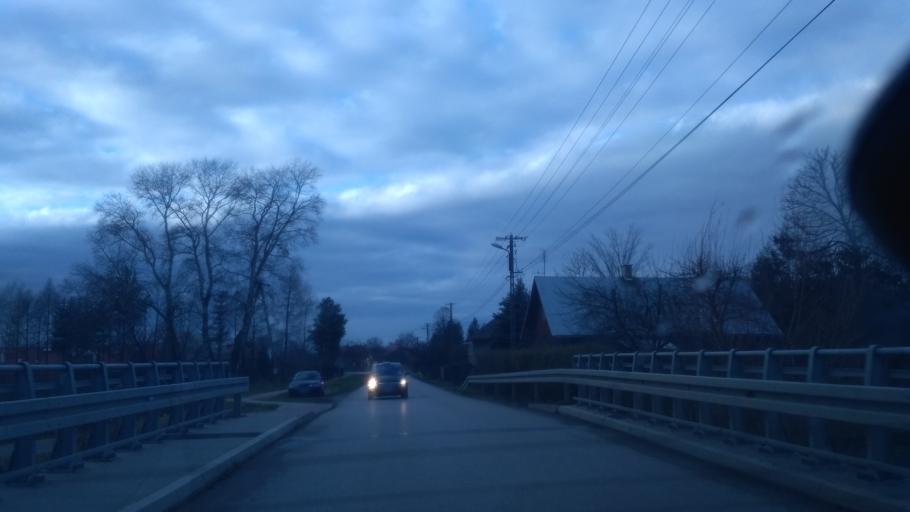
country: PL
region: Subcarpathian Voivodeship
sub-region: Powiat lancucki
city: Gluchow
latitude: 50.1006
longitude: 22.2766
